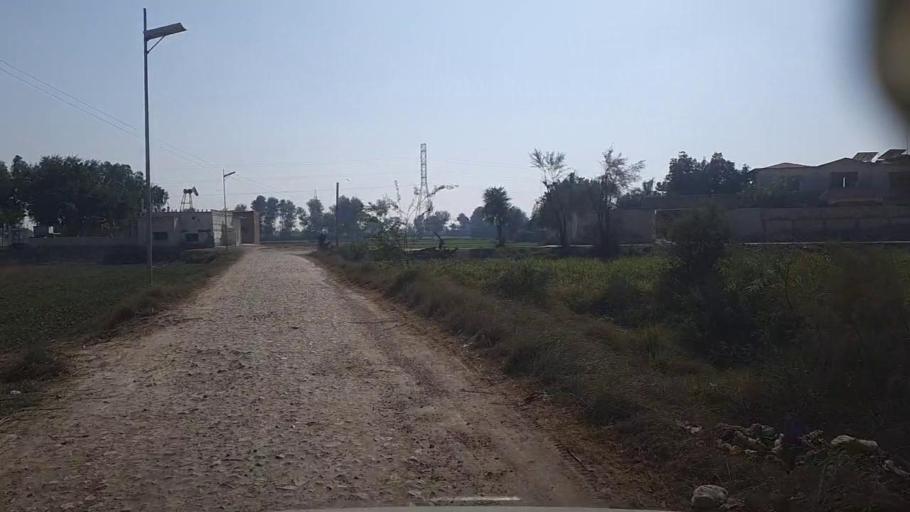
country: PK
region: Sindh
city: Khairpur
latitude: 28.0579
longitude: 69.6512
